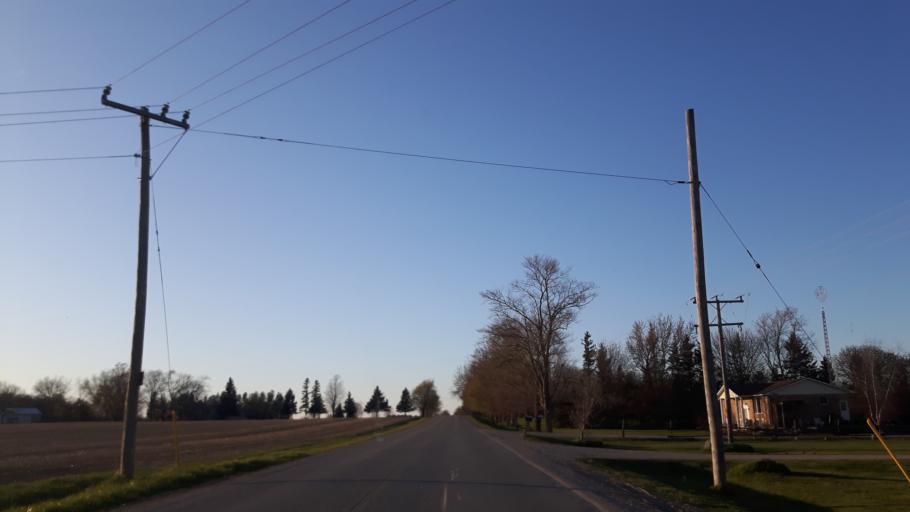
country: CA
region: Ontario
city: Bluewater
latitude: 43.5233
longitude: -81.5426
